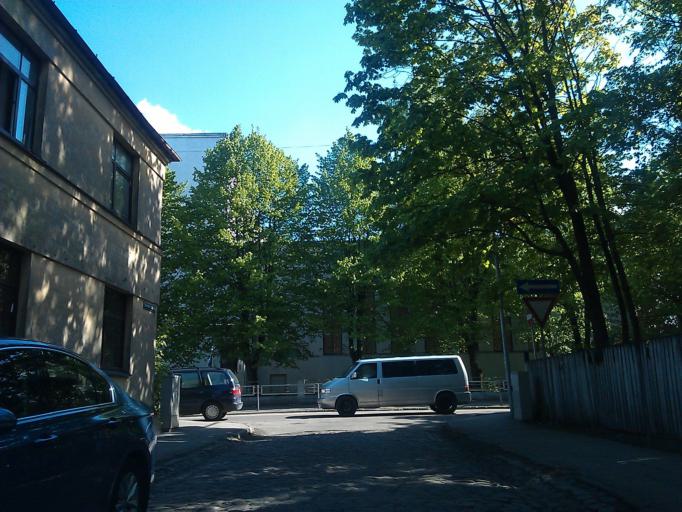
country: LV
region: Riga
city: Jaunciems
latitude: 56.9835
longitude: 24.1764
